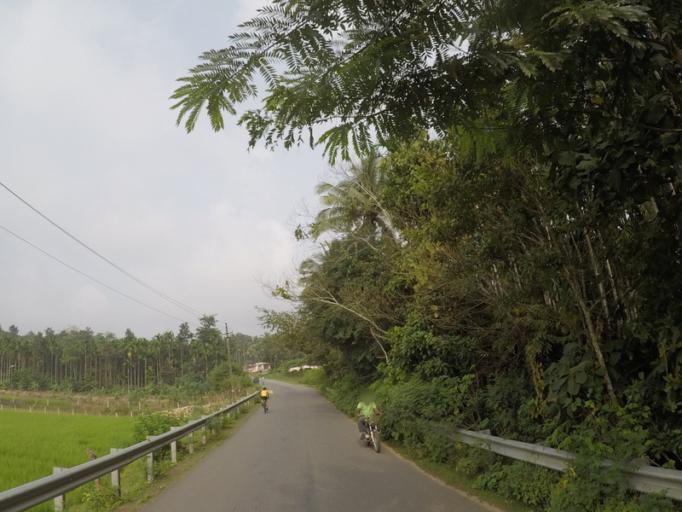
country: IN
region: Karnataka
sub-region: Chikmagalur
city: Koppa
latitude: 13.3652
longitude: 75.5149
